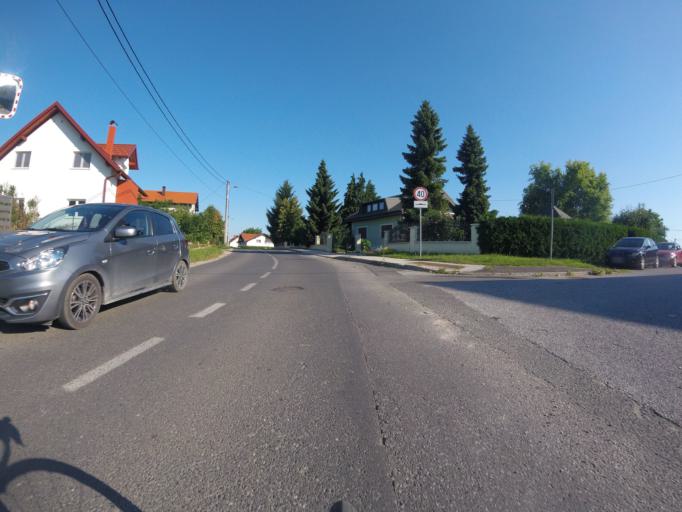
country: HR
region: Grad Zagreb
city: Zadvorsko
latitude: 45.7254
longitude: 15.9191
